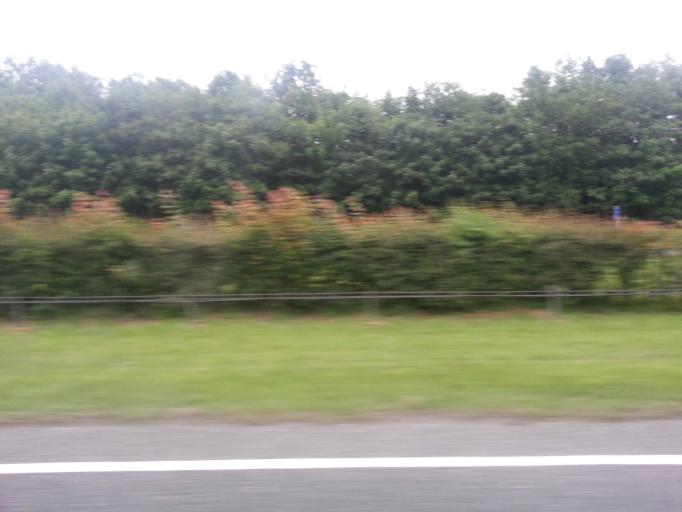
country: IE
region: Leinster
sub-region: Kildare
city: Kilcullen
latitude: 53.1819
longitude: -6.7377
